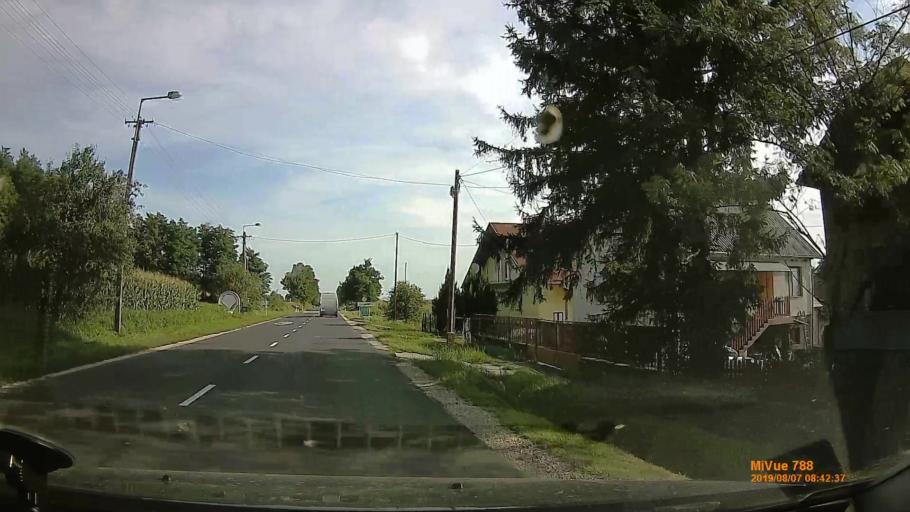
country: HU
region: Zala
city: Pacsa
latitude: 46.6011
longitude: 16.9187
